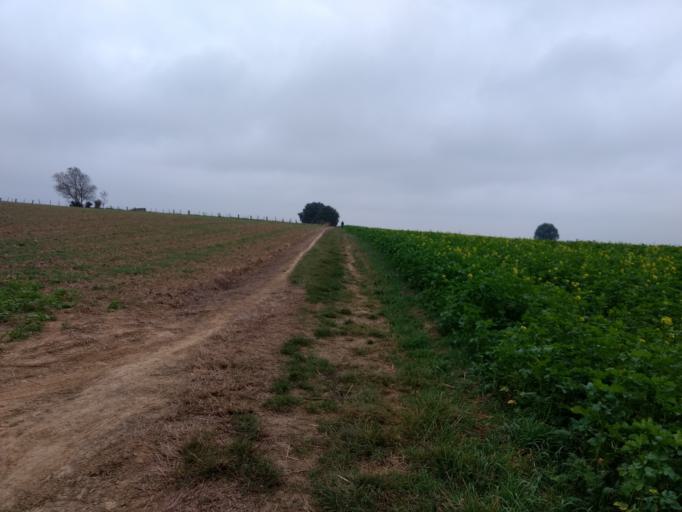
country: BE
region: Flanders
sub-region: Provincie Vlaams-Brabant
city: Bertem
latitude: 50.8764
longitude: 4.6478
